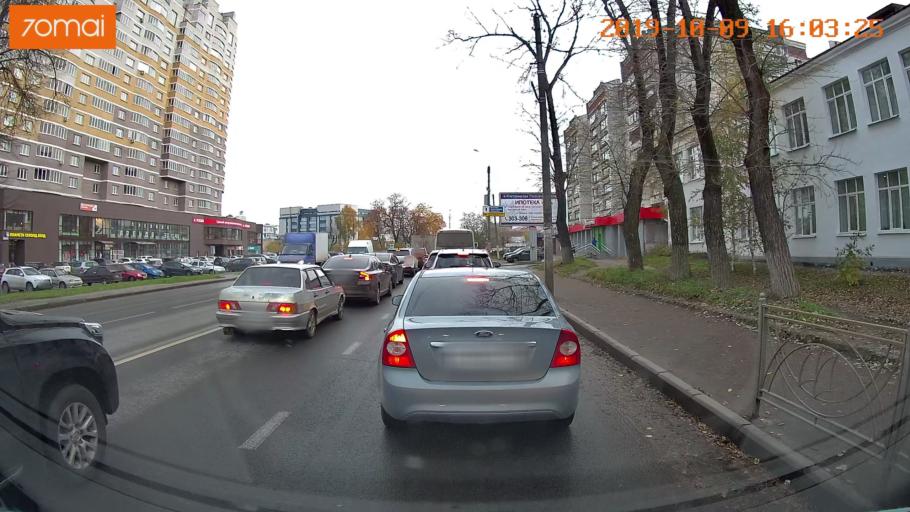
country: RU
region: Kostroma
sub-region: Kostromskoy Rayon
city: Kostroma
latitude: 57.7648
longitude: 40.9512
